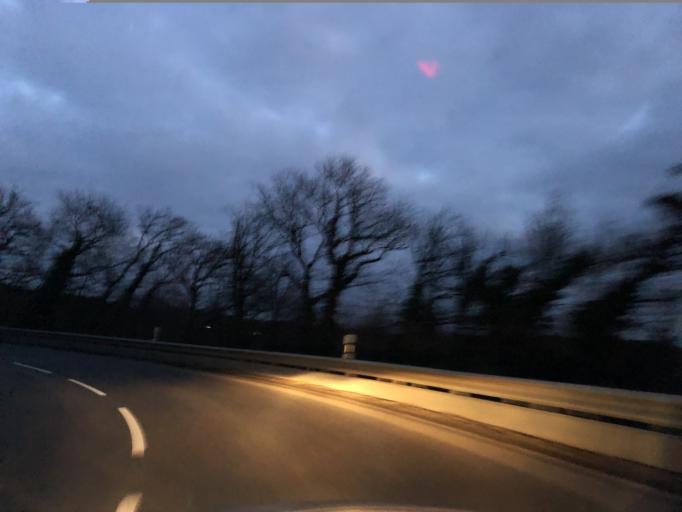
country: DE
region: Rheinland-Pfalz
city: Nassau
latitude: 50.2980
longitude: 7.8110
